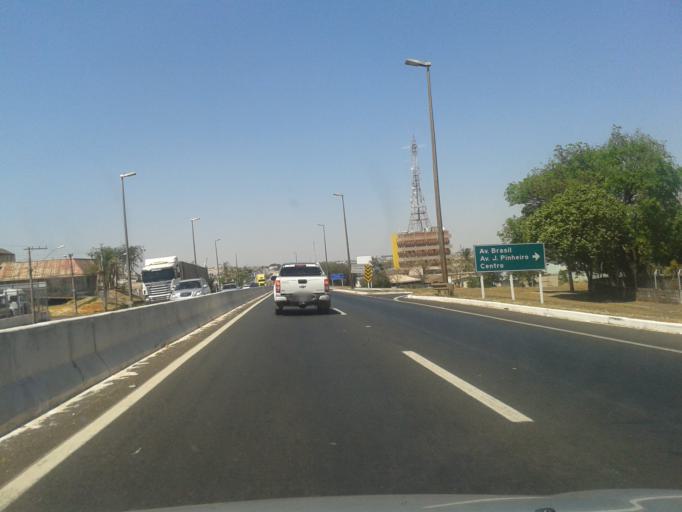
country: BR
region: Minas Gerais
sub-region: Uberlandia
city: Uberlandia
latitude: -18.8881
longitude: -48.2605
